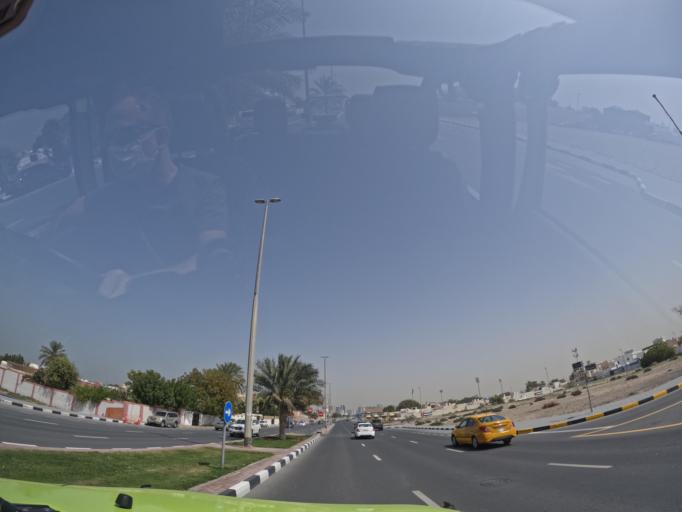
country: AE
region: Ash Shariqah
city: Sharjah
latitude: 25.3718
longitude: 55.4173
